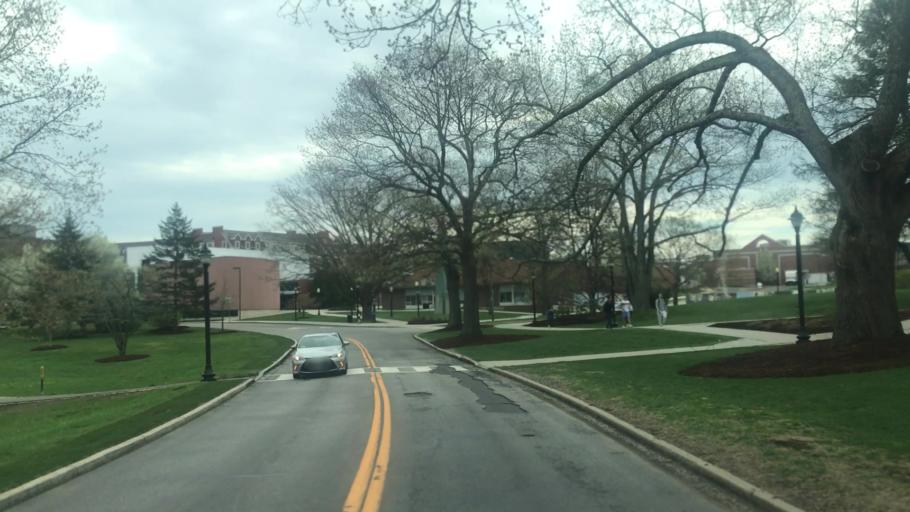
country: US
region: Connecticut
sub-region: Tolland County
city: Storrs
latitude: 41.8058
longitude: -72.2472
